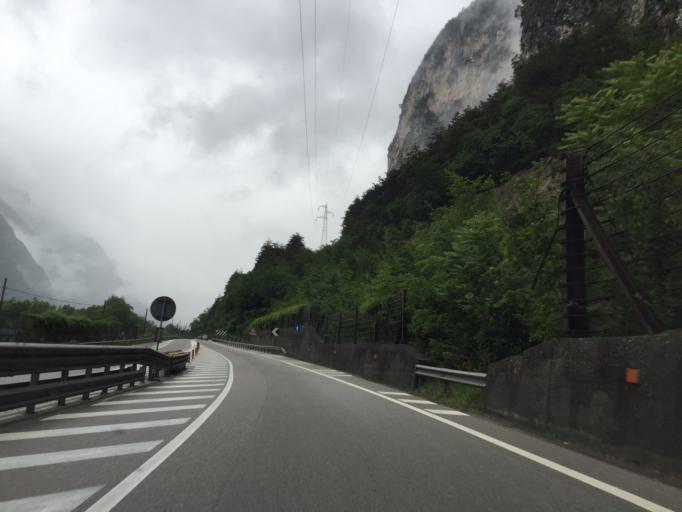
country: IT
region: Trentino-Alto Adige
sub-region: Provincia di Trento
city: Grigno
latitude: 46.0194
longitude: 11.6074
